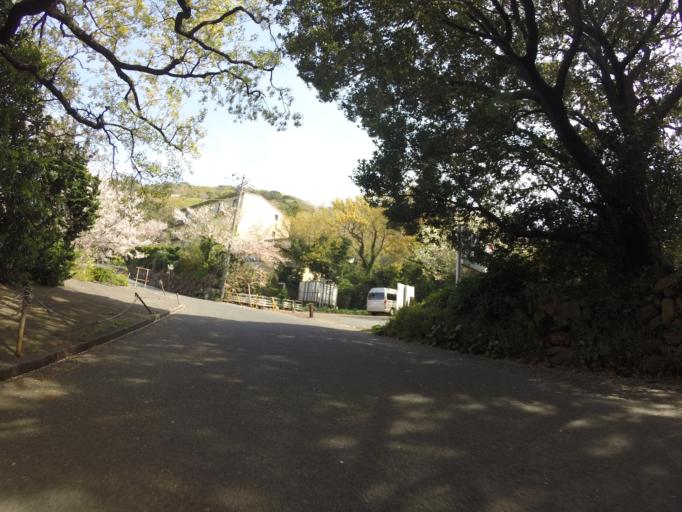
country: JP
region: Shizuoka
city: Heda
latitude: 35.0231
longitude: 138.7866
